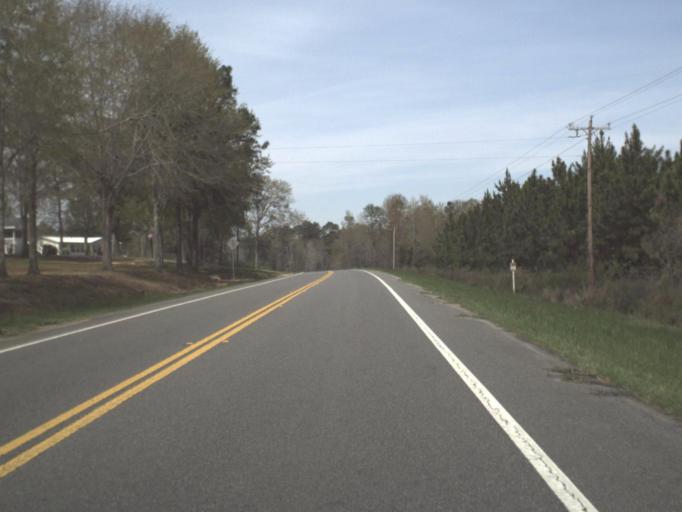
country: US
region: Alabama
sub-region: Geneva County
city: Geneva
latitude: 30.9338
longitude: -85.9670
